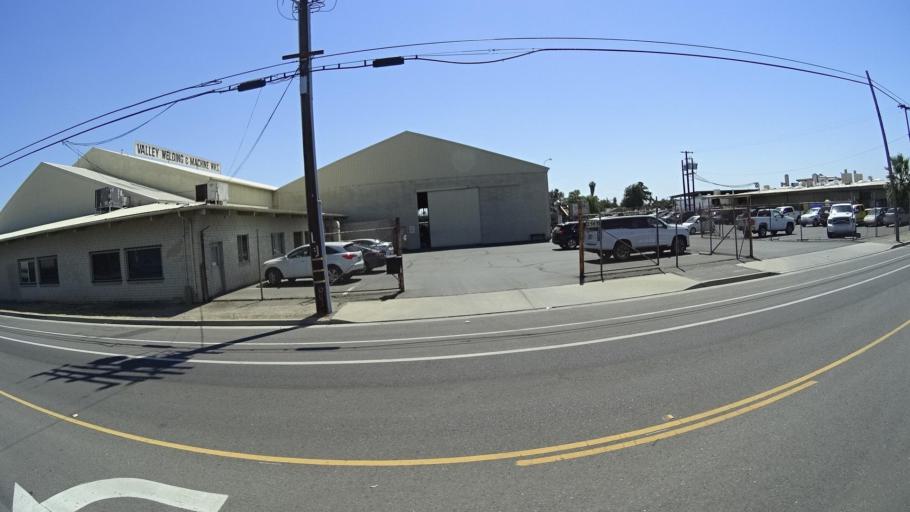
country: US
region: California
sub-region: Fresno County
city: Fresno
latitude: 36.7092
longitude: -119.7638
